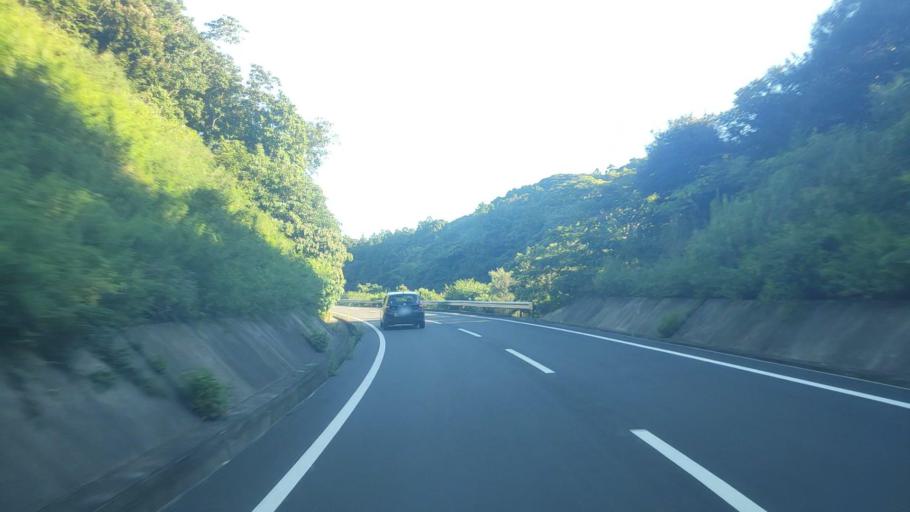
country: JP
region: Mie
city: Toba
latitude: 34.3096
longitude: 136.8800
